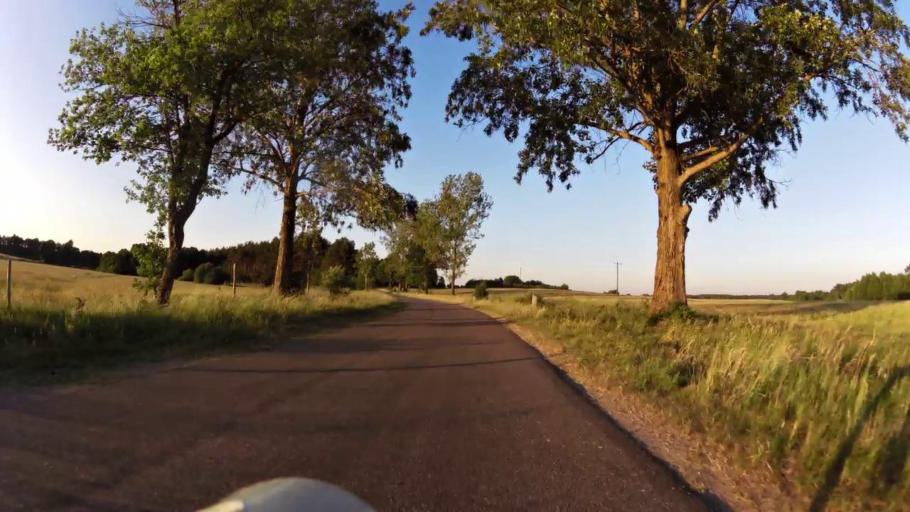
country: PL
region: West Pomeranian Voivodeship
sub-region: Powiat szczecinecki
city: Bialy Bor
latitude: 53.8518
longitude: 16.7076
